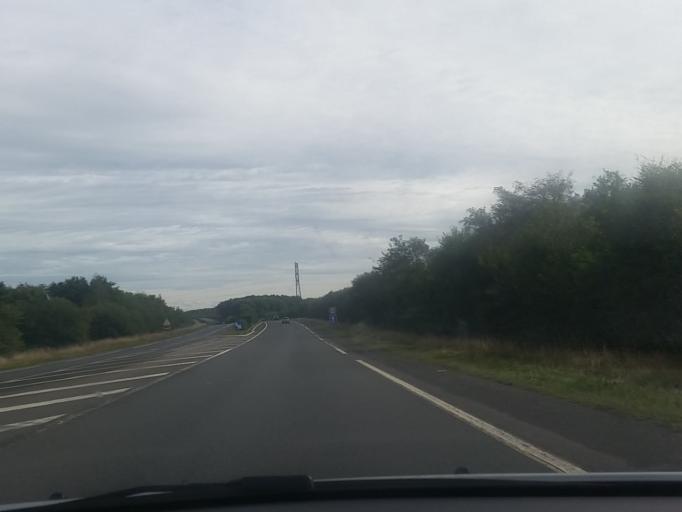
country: FR
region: Pays de la Loire
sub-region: Departement de la Loire-Atlantique
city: Saint-Aubin-des-Chateaux
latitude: 47.6851
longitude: -1.4394
